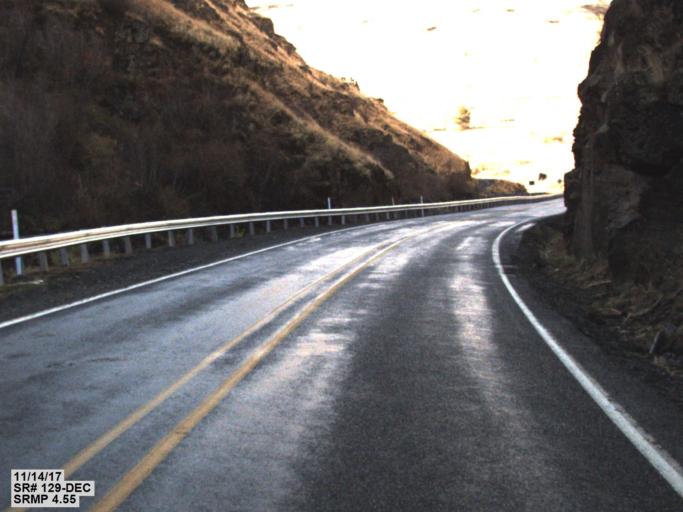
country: US
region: Washington
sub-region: Asotin County
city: Asotin
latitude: 46.0423
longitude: -117.2489
